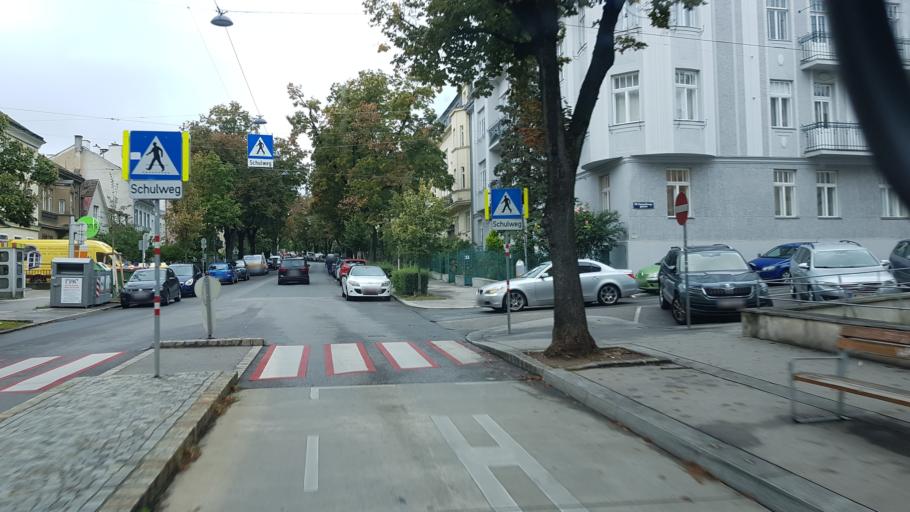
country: AT
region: Vienna
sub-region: Wien Stadt
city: Vienna
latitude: 48.2462
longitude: 16.3392
